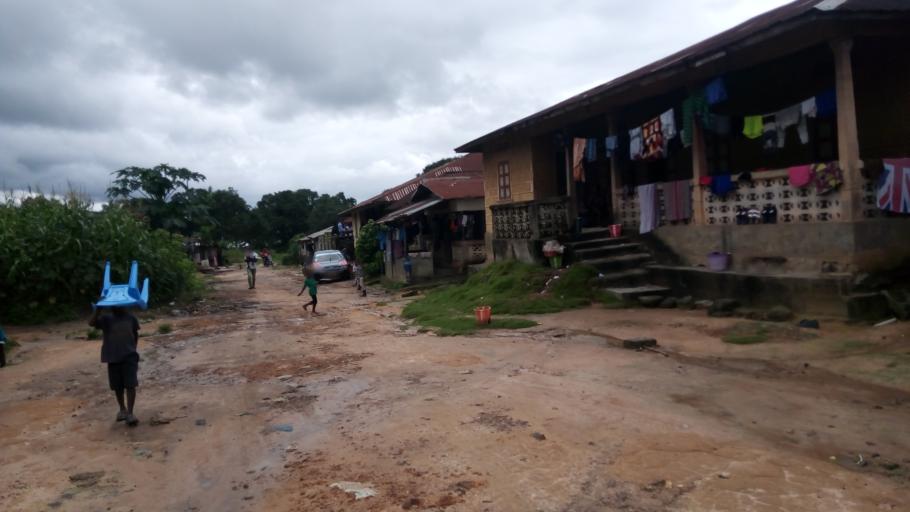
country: SL
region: Northern Province
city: Lunsar
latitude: 8.6905
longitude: -12.5353
